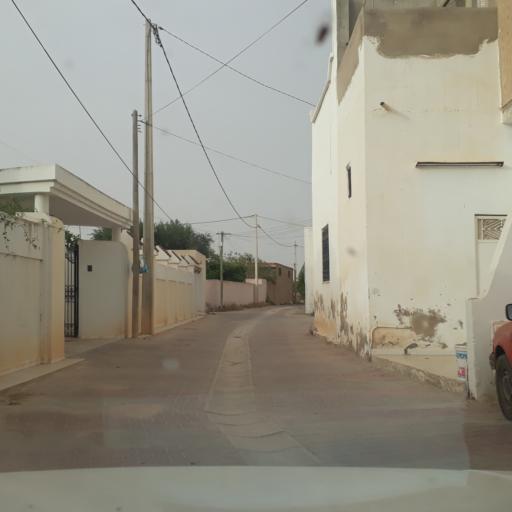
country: TN
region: Safaqis
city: Al Qarmadah
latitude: 34.8148
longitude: 10.7700
